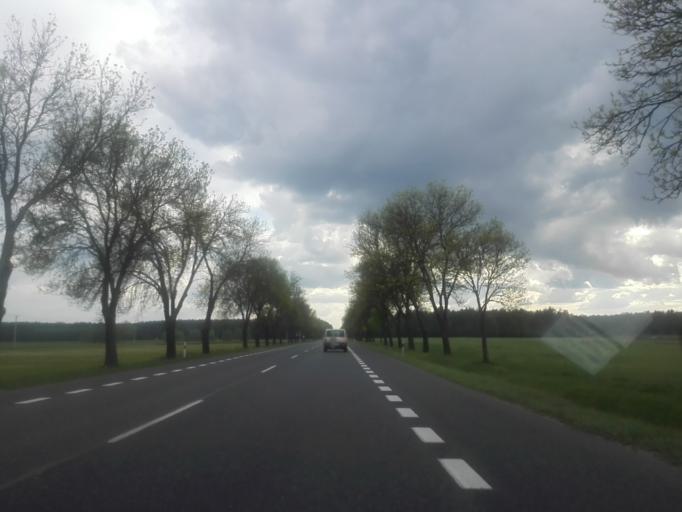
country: PL
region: Podlasie
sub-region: Powiat zambrowski
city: Szumowo
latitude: 52.8565
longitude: 21.9937
